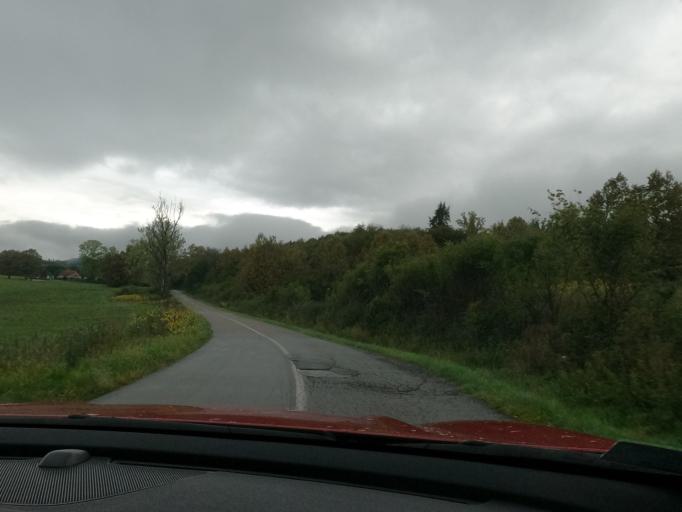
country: HR
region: Sisacko-Moslavacka
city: Glina
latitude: 45.2981
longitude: 16.1421
